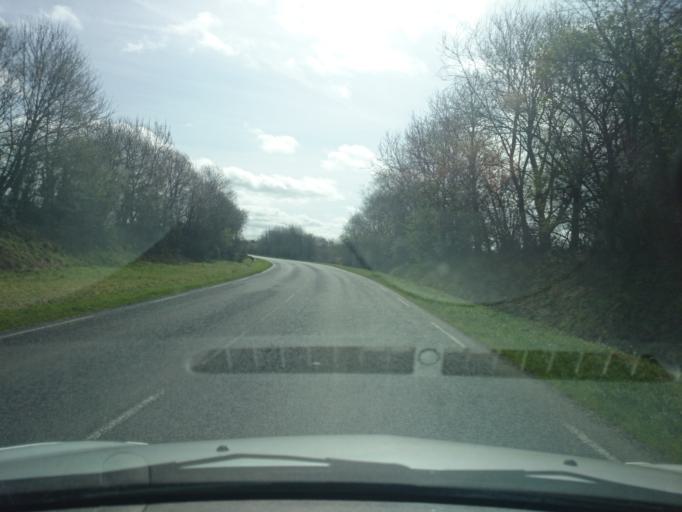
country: FR
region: Brittany
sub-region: Departement du Finistere
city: Gouesnou
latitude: 48.4392
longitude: -4.4556
